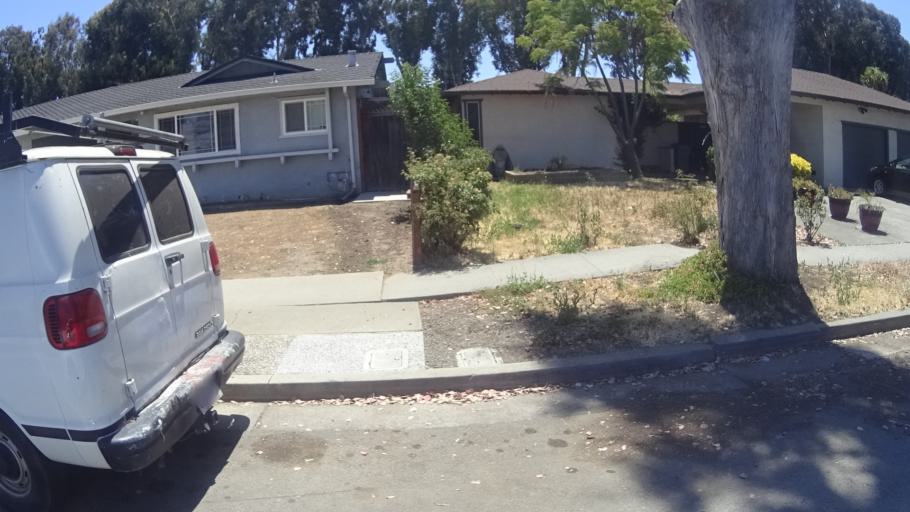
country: US
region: California
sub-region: Santa Clara County
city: Seven Trees
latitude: 37.2522
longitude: -121.8567
